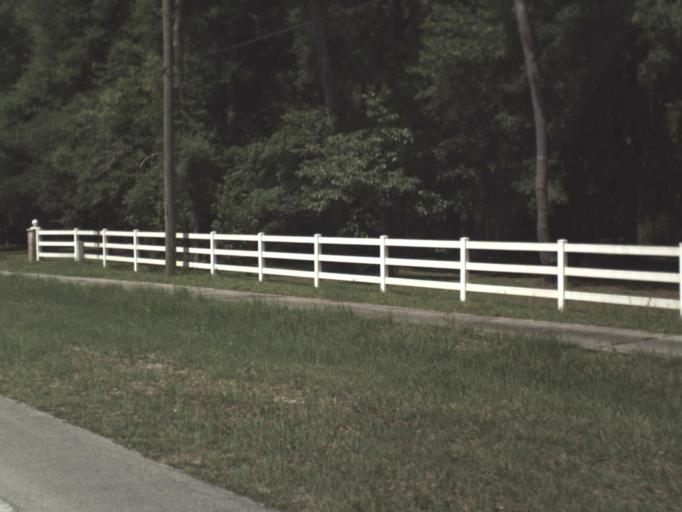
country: US
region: Florida
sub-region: Bradford County
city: Starke
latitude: 29.9594
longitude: -82.0163
